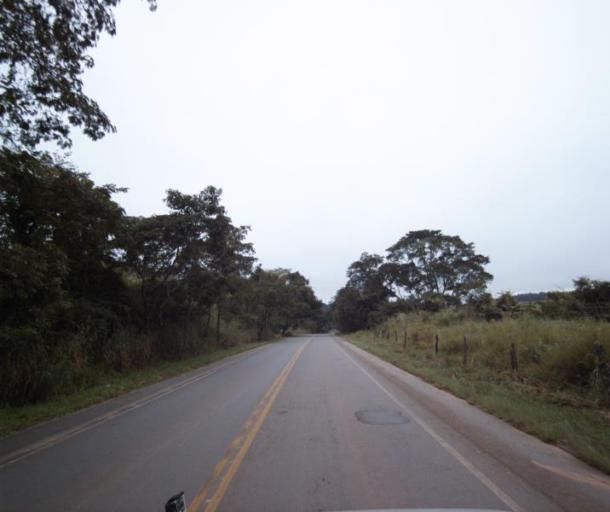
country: BR
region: Goias
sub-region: Pirenopolis
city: Pirenopolis
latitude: -15.9620
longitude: -48.8184
